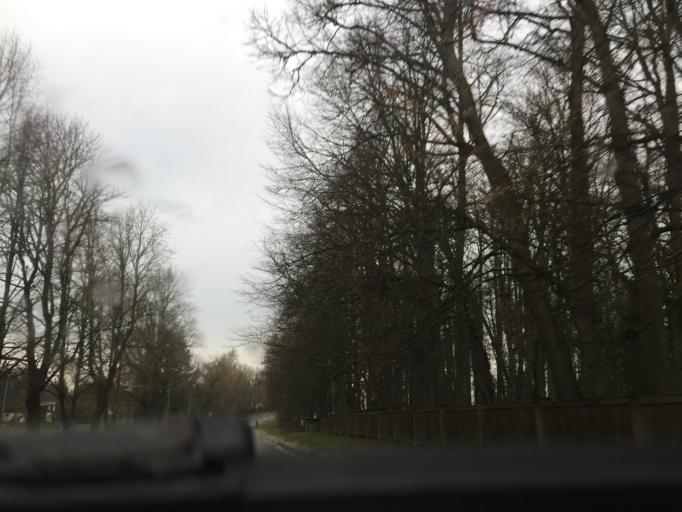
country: EE
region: Tartu
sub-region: UElenurme vald
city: Ulenurme
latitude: 58.3157
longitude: 26.7213
